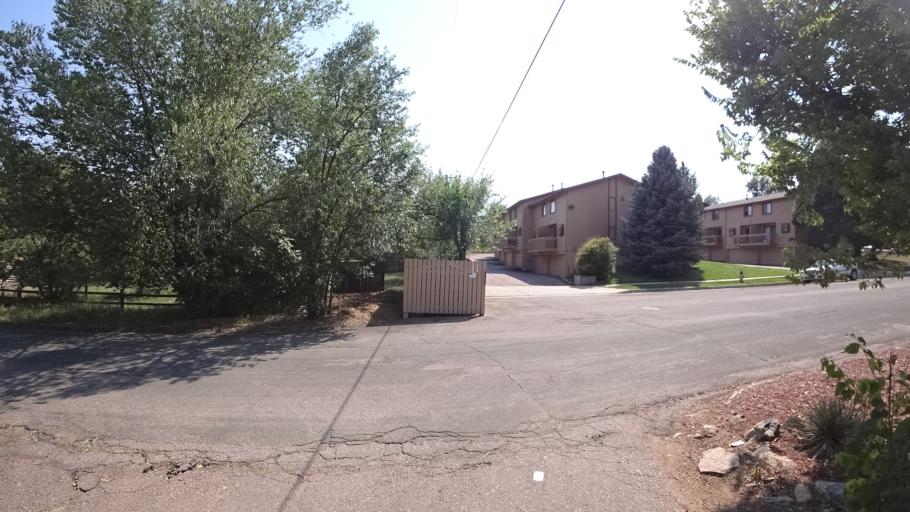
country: US
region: Colorado
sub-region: El Paso County
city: Colorado Springs
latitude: 38.8031
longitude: -104.8248
